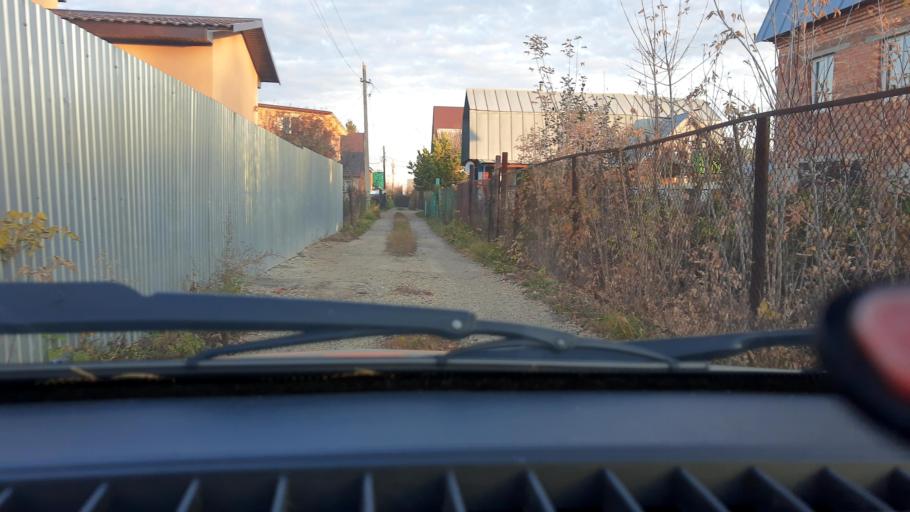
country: RU
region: Bashkortostan
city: Ufa
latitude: 54.6885
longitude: 55.9010
